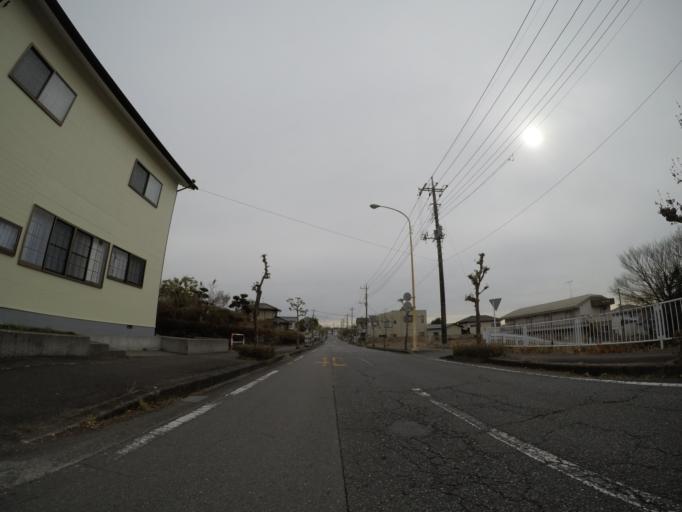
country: JP
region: Shizuoka
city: Fujinomiya
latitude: 35.2529
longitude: 138.6353
